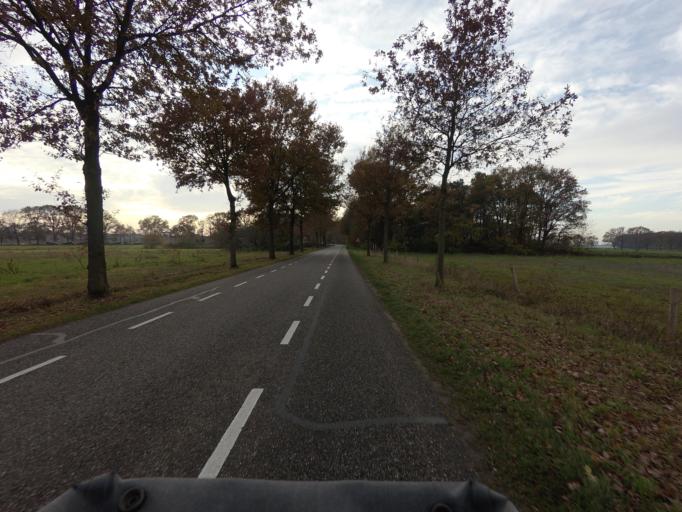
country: NL
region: North Brabant
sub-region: Gemeente Breda
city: Breda
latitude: 51.5023
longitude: 4.8157
